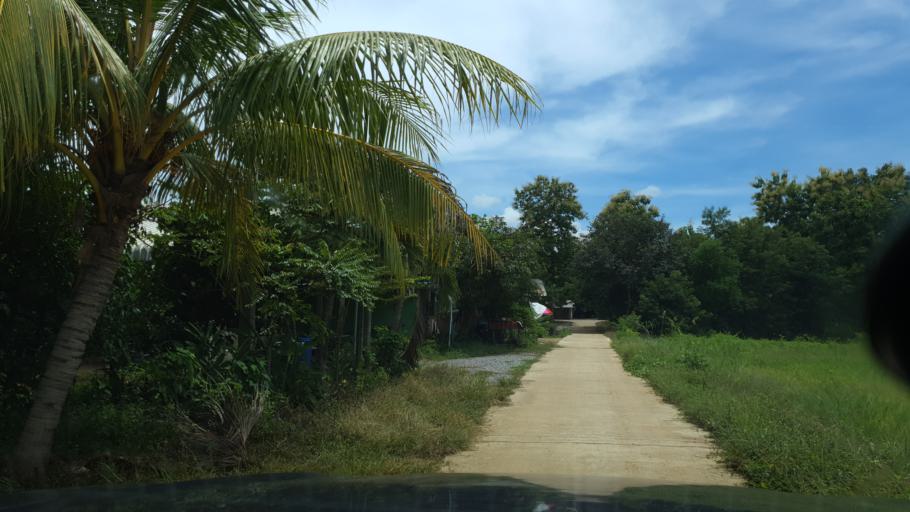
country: TH
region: Sukhothai
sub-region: Amphoe Si Satchanalai
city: Si Satchanalai
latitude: 17.6655
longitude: 99.6903
